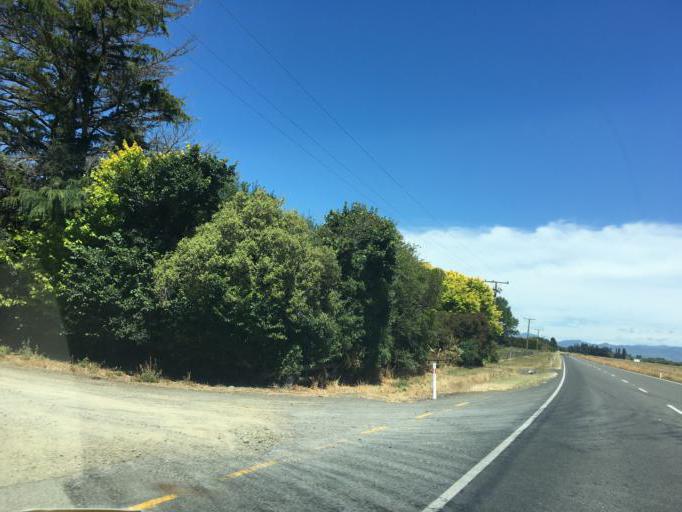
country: NZ
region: Hawke's Bay
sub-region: Hastings District
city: Hastings
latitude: -39.9967
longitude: 176.4189
